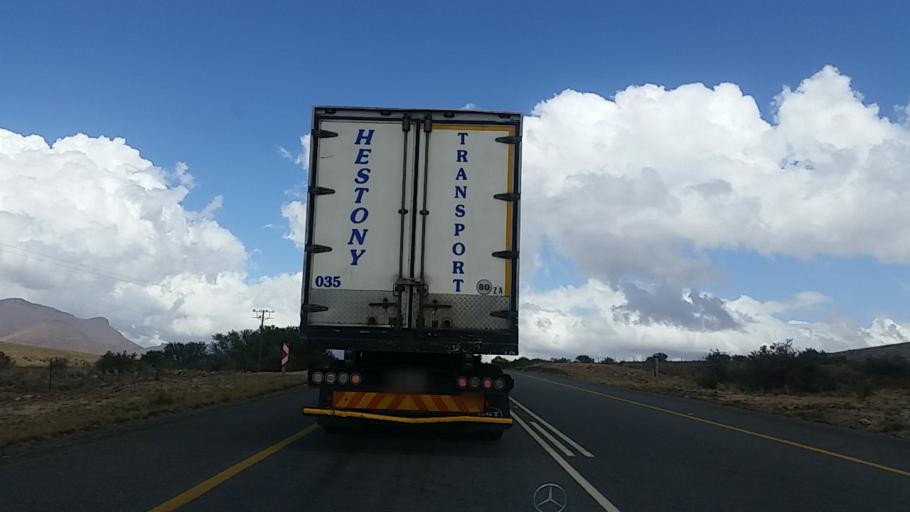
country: ZA
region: Eastern Cape
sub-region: Chris Hani District Municipality
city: Middelburg
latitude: -31.7325
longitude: 24.9451
